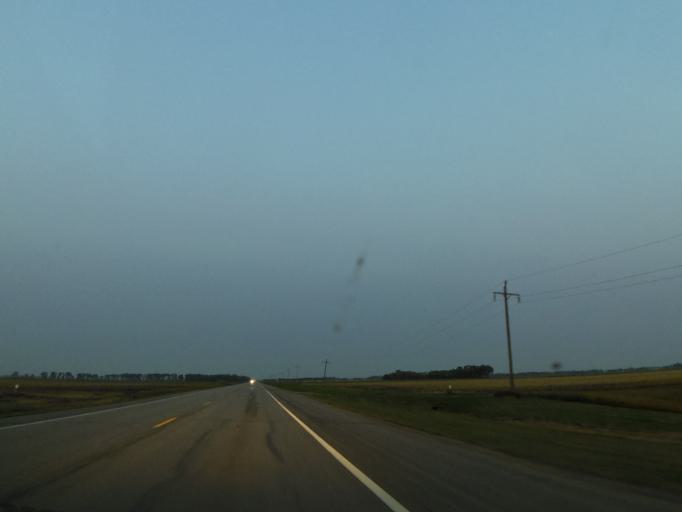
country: US
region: North Dakota
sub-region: Walsh County
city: Grafton
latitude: 48.4119
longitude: -97.2459
